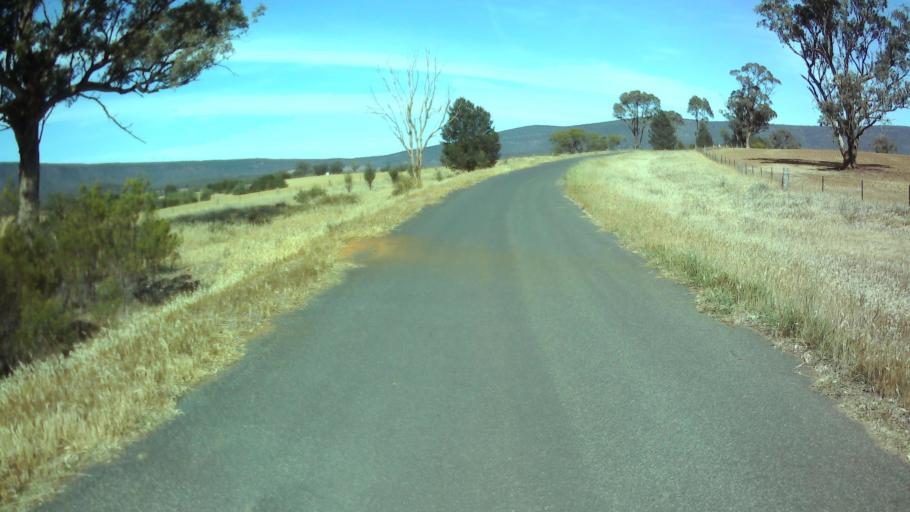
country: AU
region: New South Wales
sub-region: Weddin
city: Grenfell
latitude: -33.9410
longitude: 148.0673
